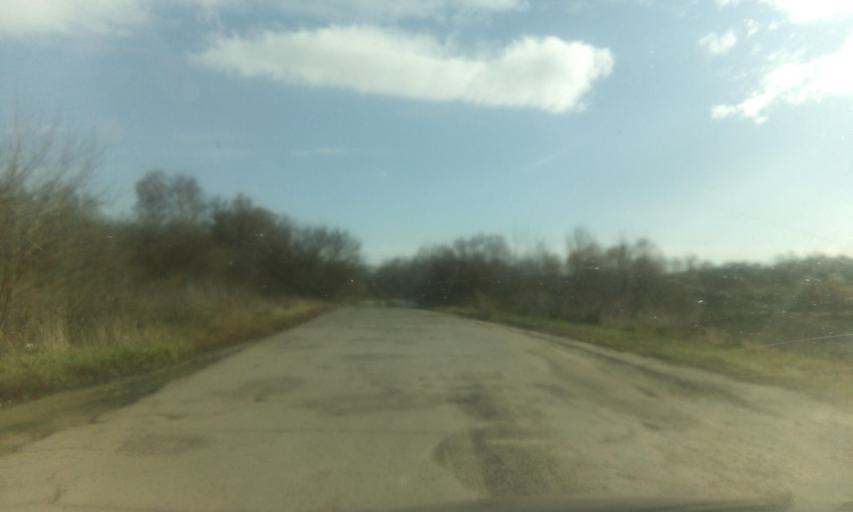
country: RU
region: Tula
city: Dubovka
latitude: 53.9489
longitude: 38.0279
